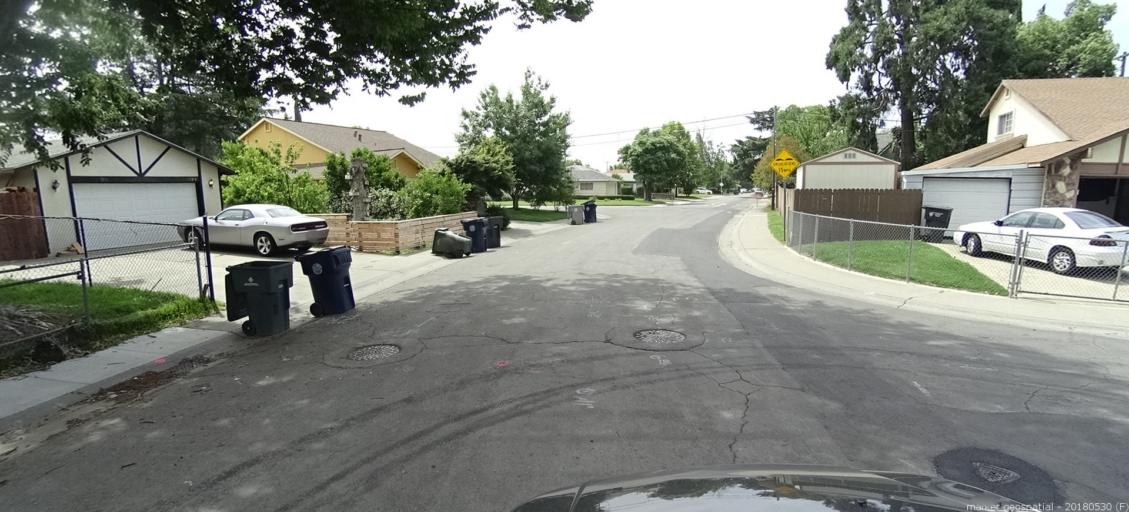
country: US
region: California
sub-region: Sacramento County
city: Sacramento
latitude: 38.6163
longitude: -121.4804
